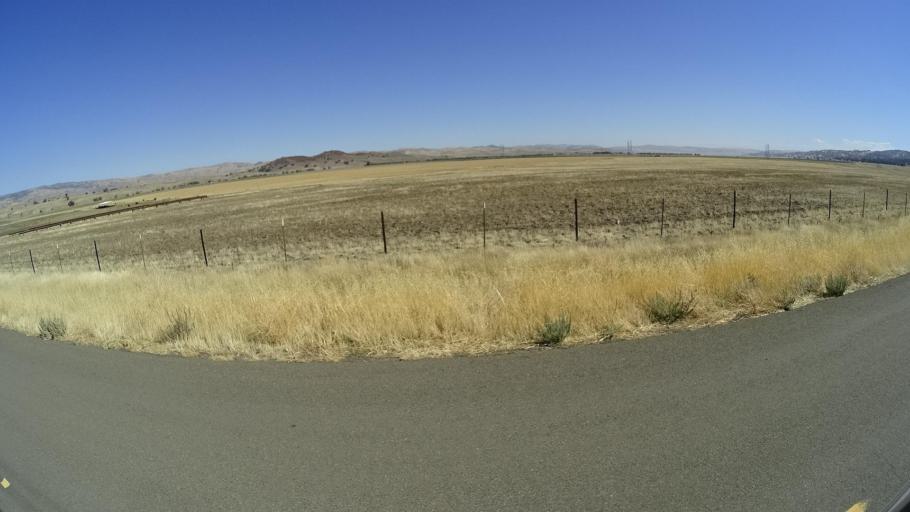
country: US
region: California
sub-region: San Luis Obispo County
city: Shandon
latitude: 35.8282
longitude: -120.3858
